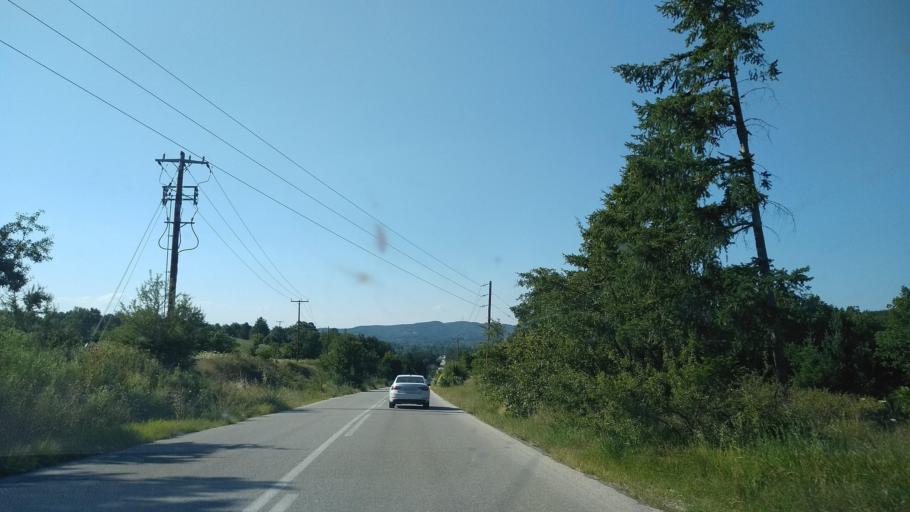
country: GR
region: Central Macedonia
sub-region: Nomos Chalkidikis
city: Palaiochori
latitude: 40.4644
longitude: 23.6517
